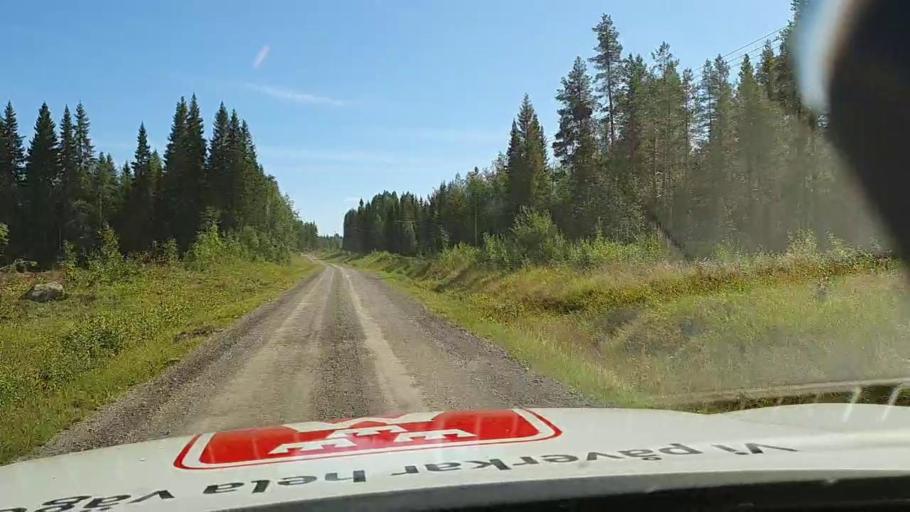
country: SE
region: Jaemtland
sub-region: Stroemsunds Kommun
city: Stroemsund
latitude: 63.7593
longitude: 15.3564
